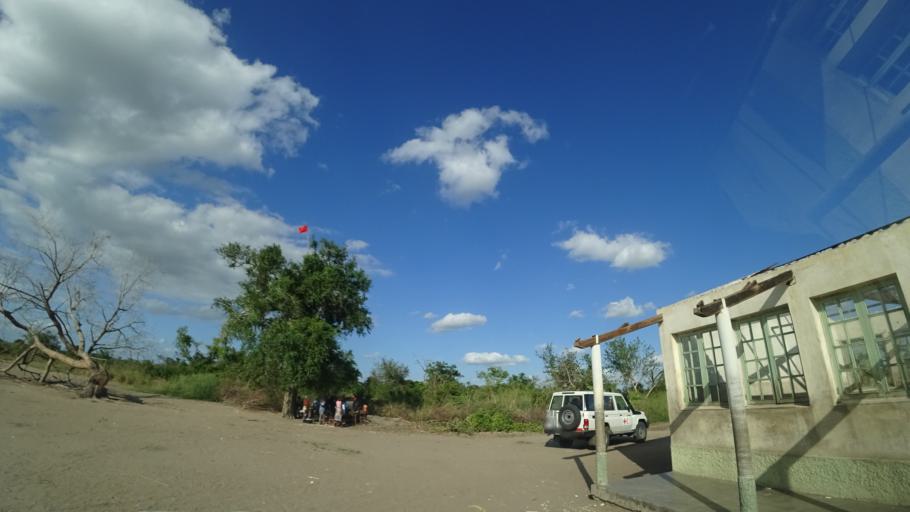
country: MZ
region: Sofala
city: Dondo
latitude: -19.3366
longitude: 34.5821
